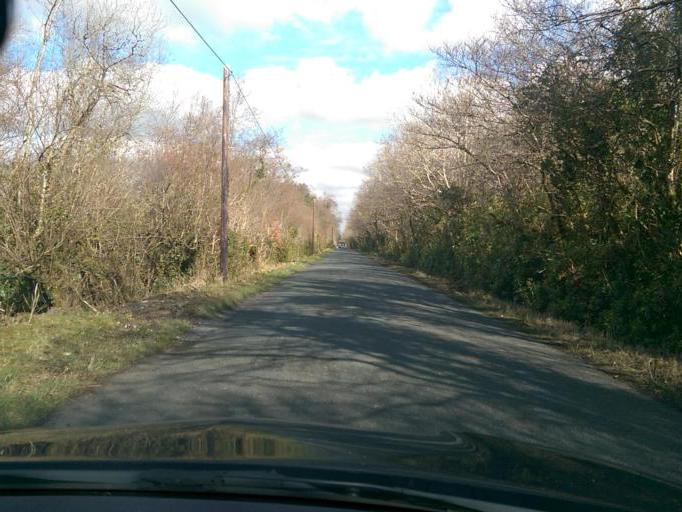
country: IE
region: Connaught
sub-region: County Galway
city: Loughrea
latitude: 53.4698
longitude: -8.5254
